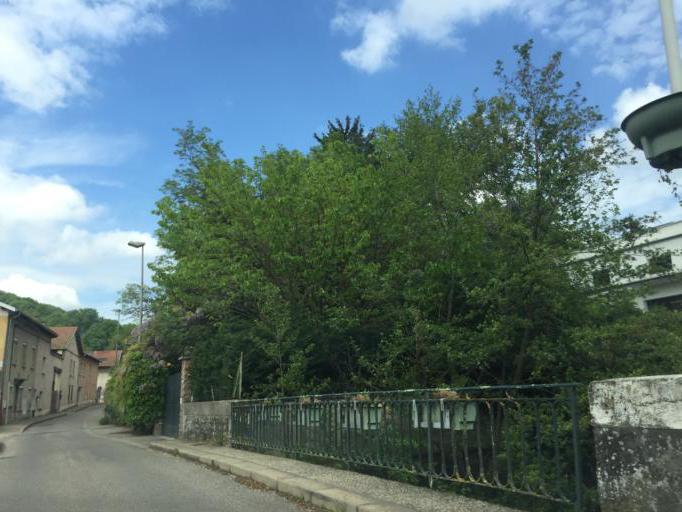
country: FR
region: Rhone-Alpes
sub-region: Departement de l'Ain
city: La Boisse
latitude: 45.8427
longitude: 5.0312
